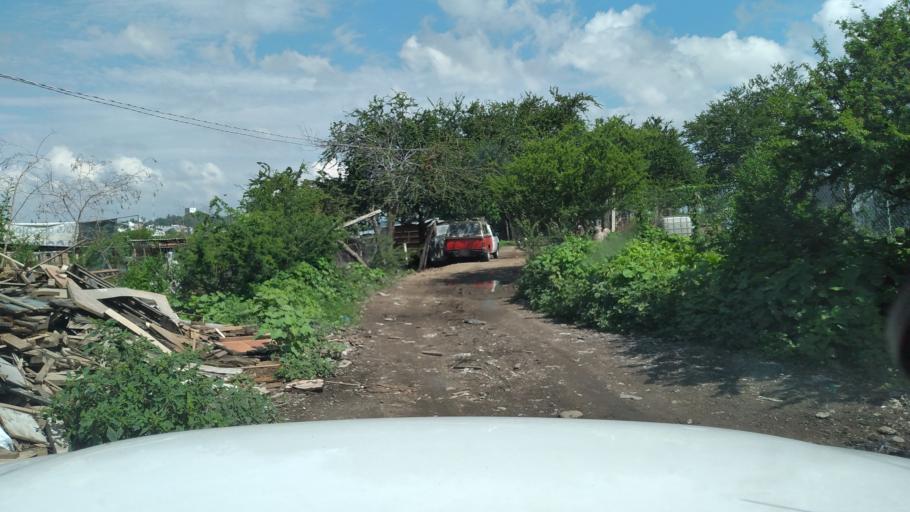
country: MX
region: Jalisco
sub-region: Zapopan
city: San Isidro
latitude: 20.7299
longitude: -103.2971
